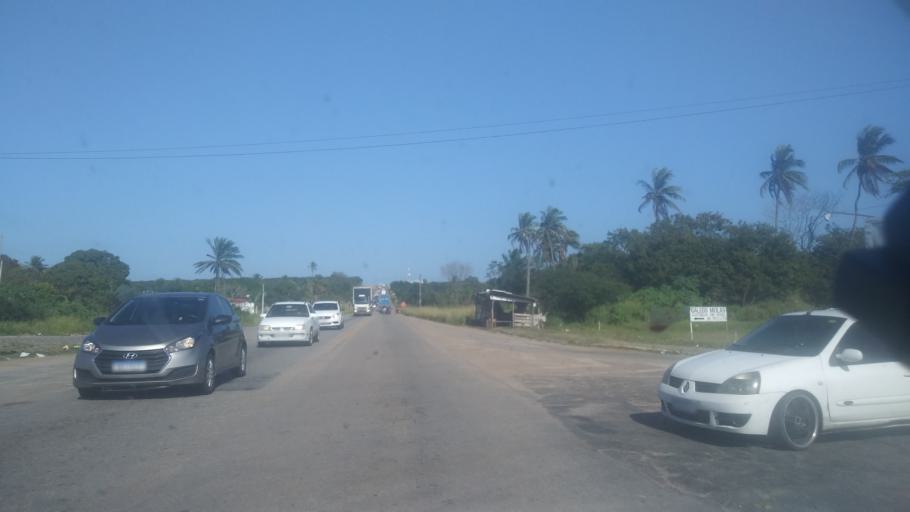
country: BR
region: Rio Grande do Norte
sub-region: Macaiba
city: Macaiba
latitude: -5.8662
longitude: -35.3595
